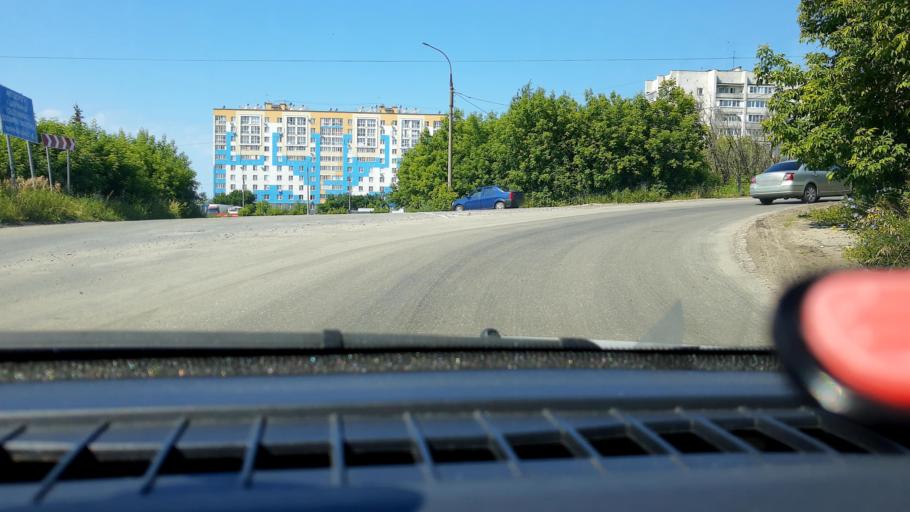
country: RU
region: Nizjnij Novgorod
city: Dzerzhinsk
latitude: 56.2329
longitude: 43.4912
